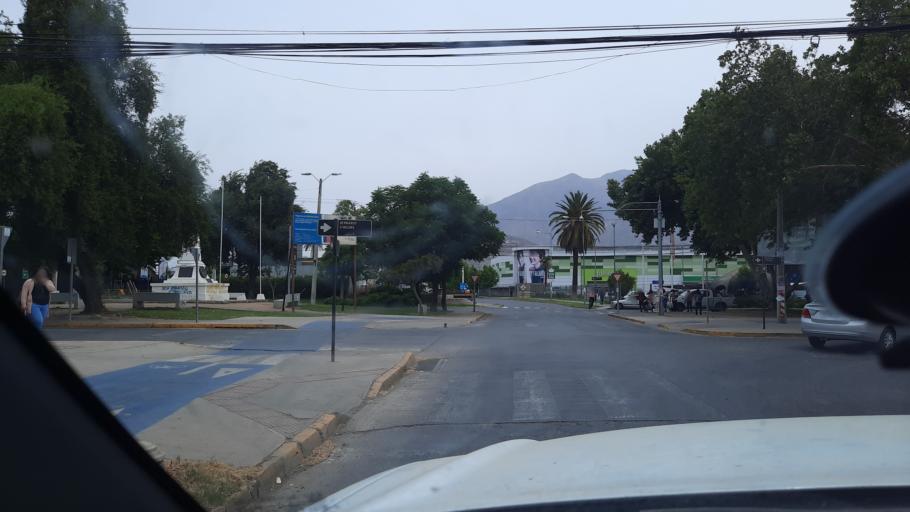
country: CL
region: Valparaiso
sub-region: Provincia de San Felipe
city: San Felipe
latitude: -32.7572
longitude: -70.7220
